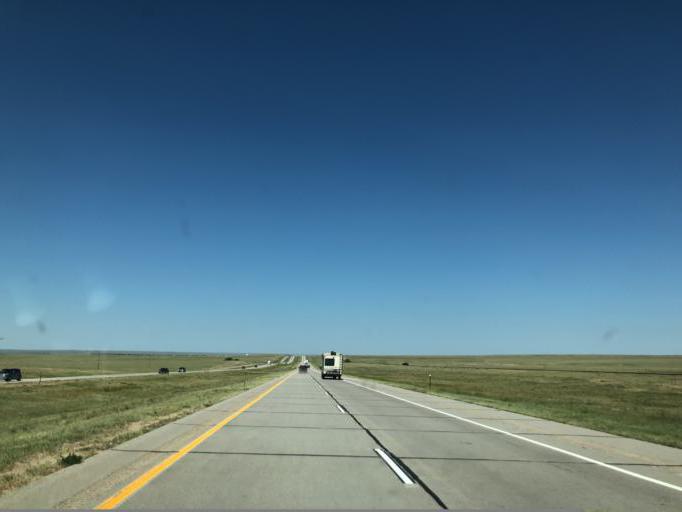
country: US
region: Colorado
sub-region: Lincoln County
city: Limon
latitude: 39.2654
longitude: -103.5689
